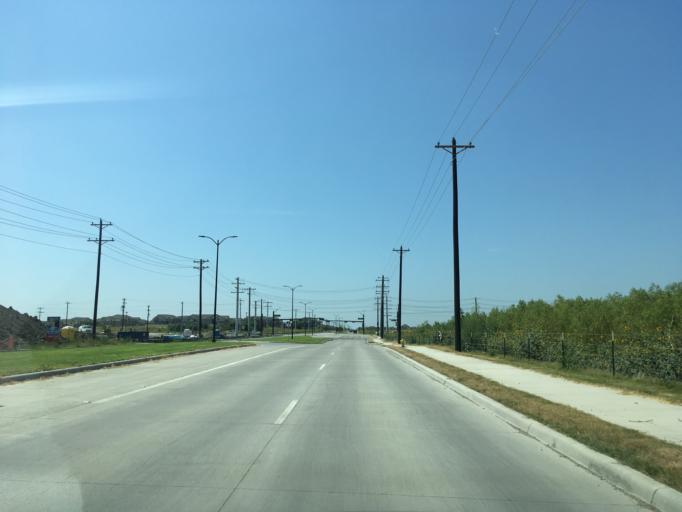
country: US
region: Texas
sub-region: Collin County
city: Prosper
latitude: 33.2060
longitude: -96.7678
